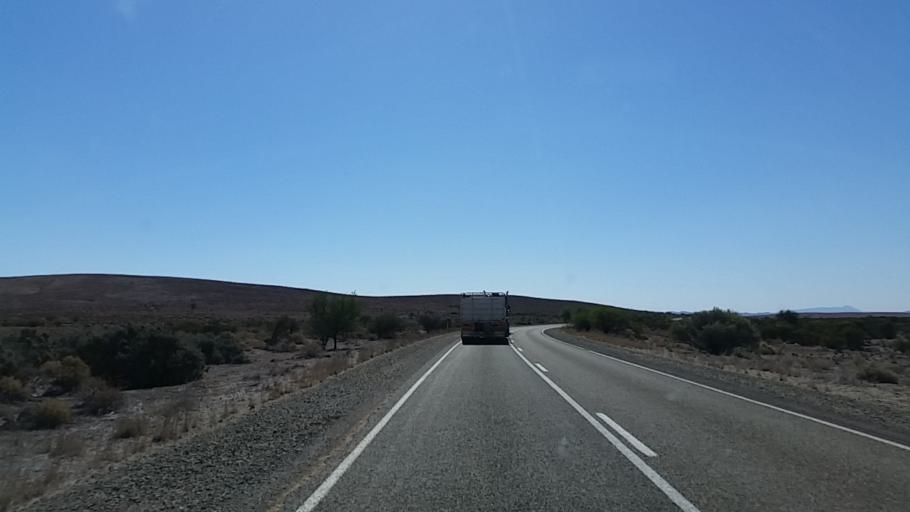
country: AU
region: South Australia
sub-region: Flinders Ranges
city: Quorn
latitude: -32.1379
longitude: 138.5149
